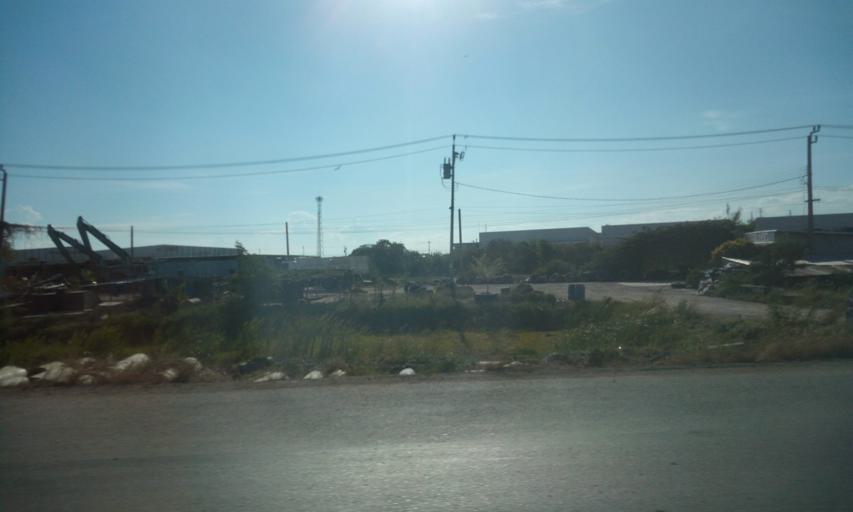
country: TH
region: Samut Prakan
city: Bang Bo District
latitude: 13.5786
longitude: 100.7577
